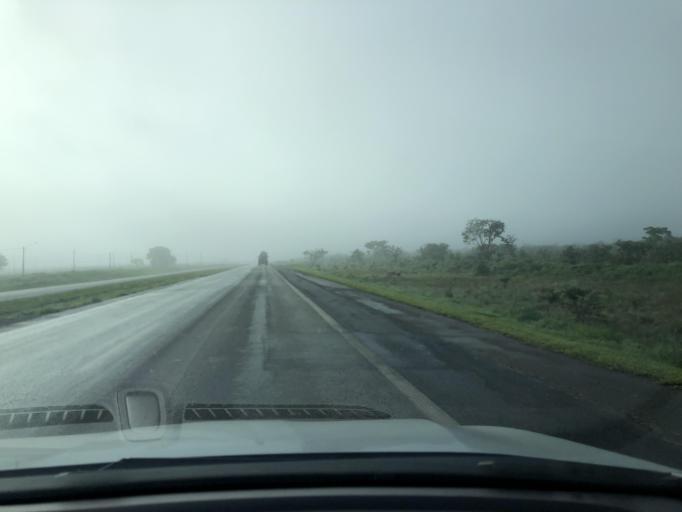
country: BR
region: Goias
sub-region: Luziania
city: Luziania
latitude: -16.2808
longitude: -47.8595
